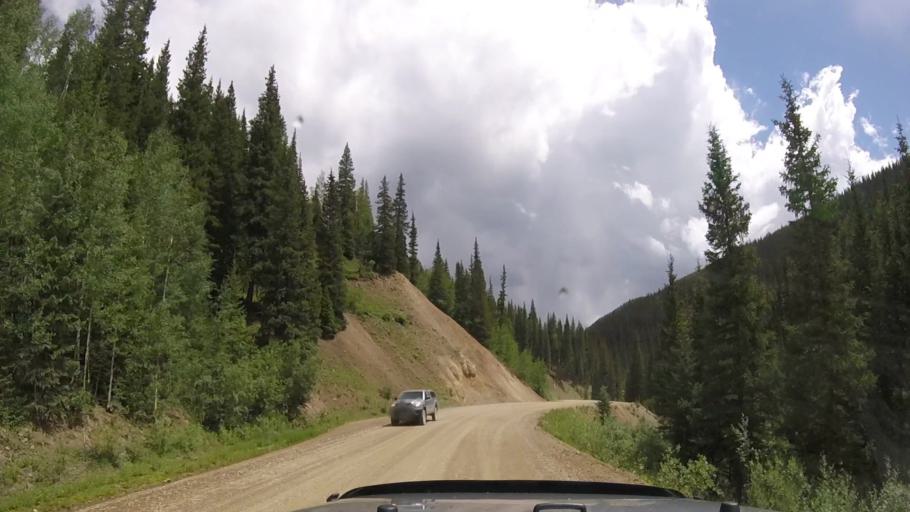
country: US
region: Colorado
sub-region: San Juan County
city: Silverton
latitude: 37.8378
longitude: -107.6783
